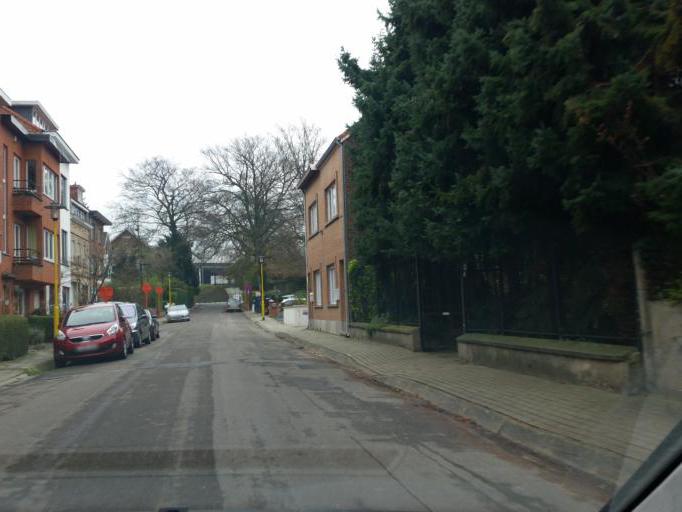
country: BE
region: Flanders
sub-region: Provincie Vlaams-Brabant
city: Bever
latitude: 50.9039
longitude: 4.3426
